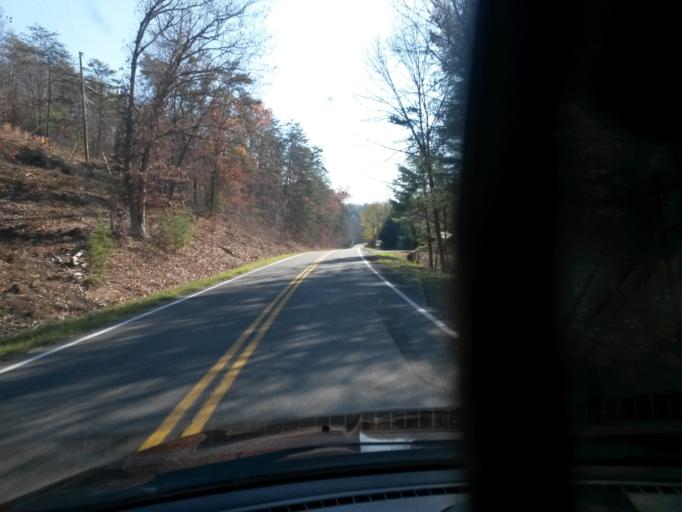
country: US
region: Virginia
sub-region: Alleghany County
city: Clifton Forge
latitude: 37.8264
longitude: -79.7568
